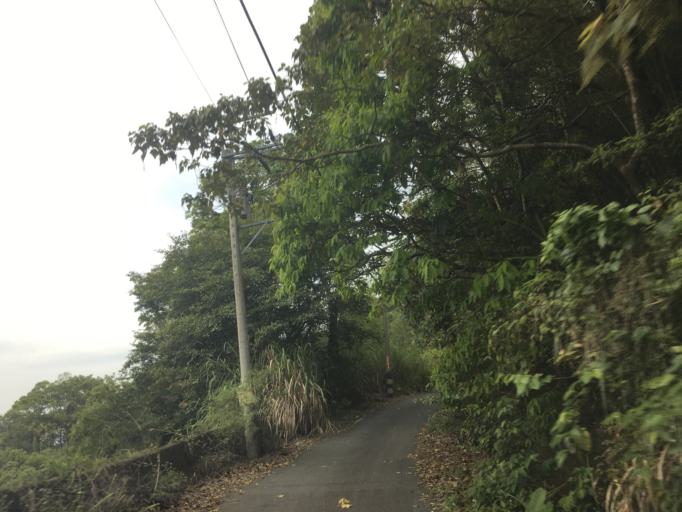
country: TW
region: Taiwan
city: Zhongxing New Village
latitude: 23.9696
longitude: 120.8224
